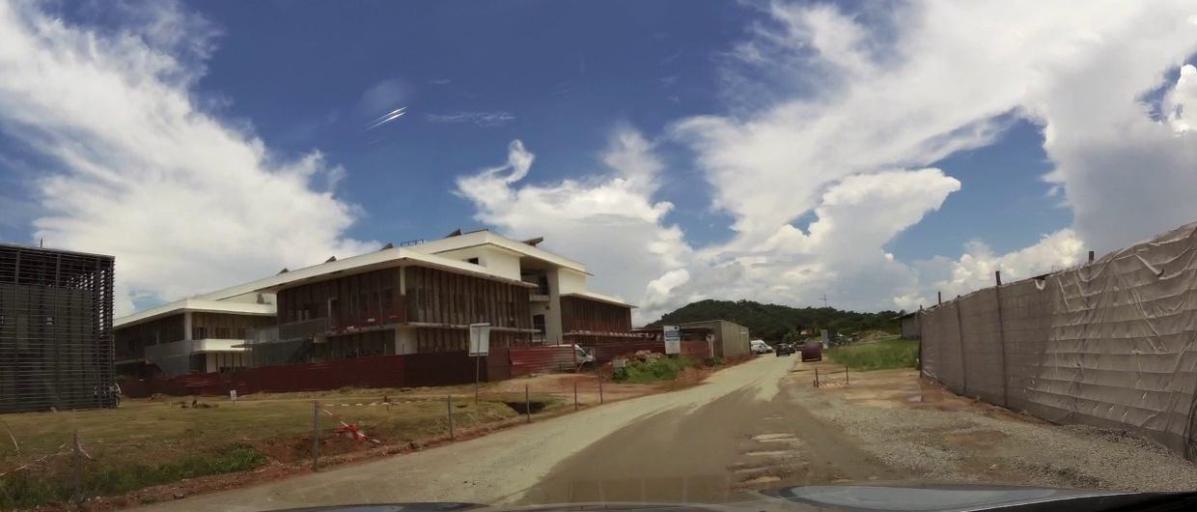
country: GF
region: Guyane
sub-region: Guyane
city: Cayenne
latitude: 4.9327
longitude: -52.3021
